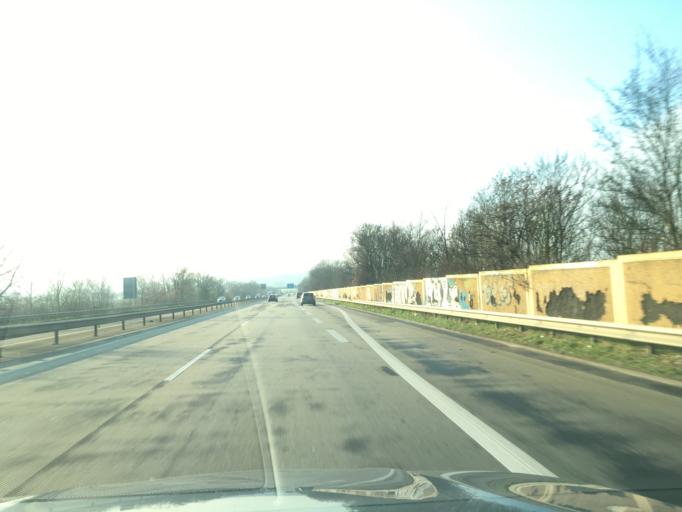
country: DE
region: Rheinland-Pfalz
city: Sankt Sebastian
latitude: 50.4064
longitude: 7.5691
